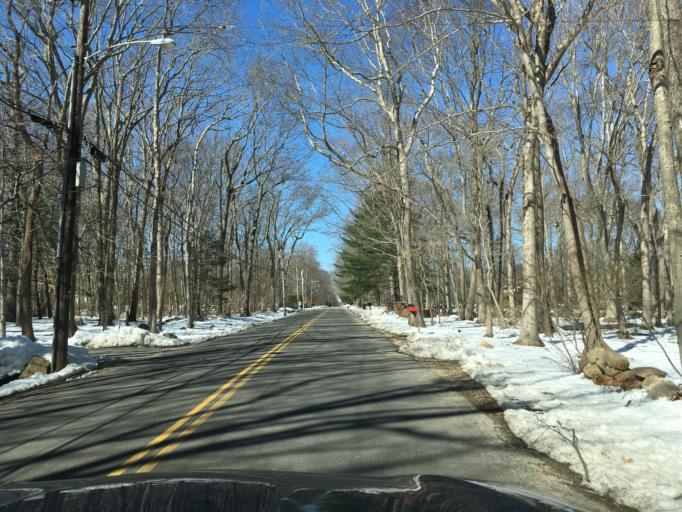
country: US
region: Rhode Island
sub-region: Washington County
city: Exeter
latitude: 41.6080
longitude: -71.5347
